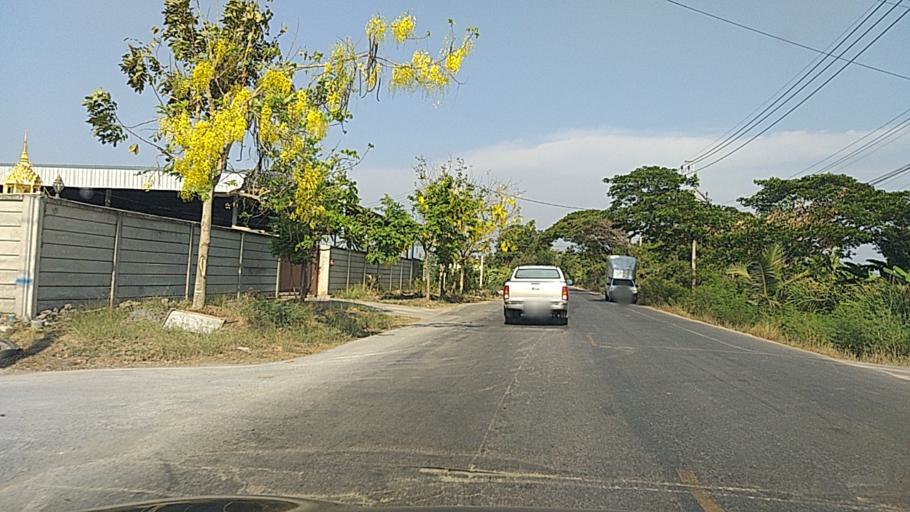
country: TH
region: Nonthaburi
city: Bang Yai
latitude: 13.8820
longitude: 100.3243
